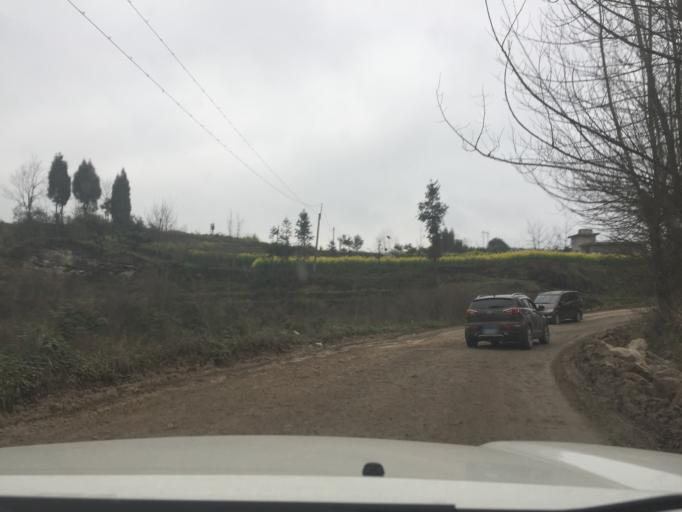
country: CN
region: Guizhou Sheng
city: Zunyi
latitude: 27.1717
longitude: 106.9144
